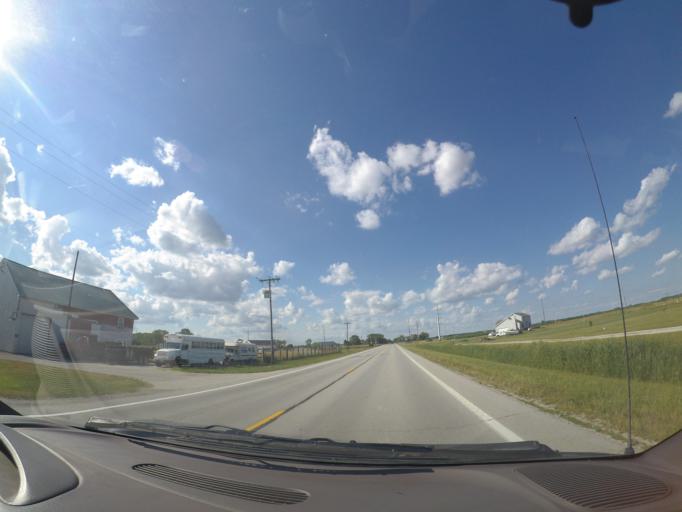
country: US
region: Ohio
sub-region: Sandusky County
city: Woodville
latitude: 41.4476
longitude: -83.4152
